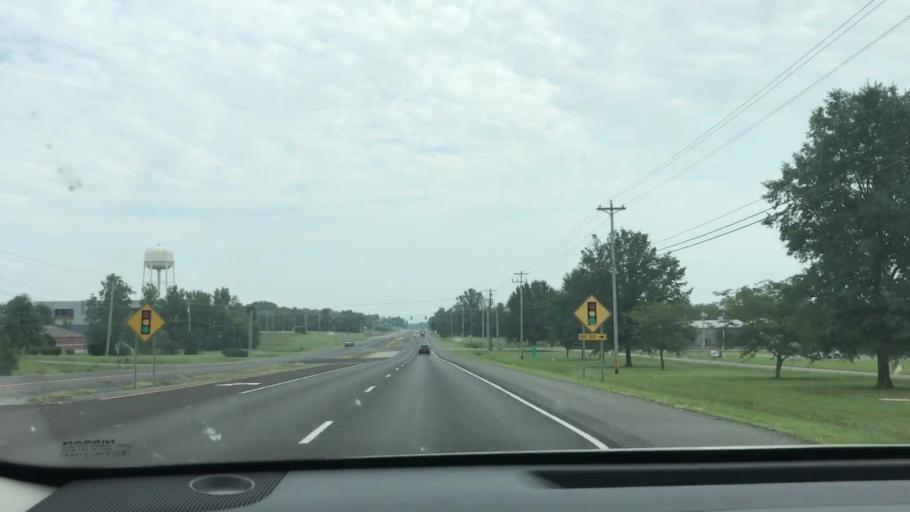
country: US
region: Kentucky
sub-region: Calloway County
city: Murray
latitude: 36.6568
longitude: -88.3069
